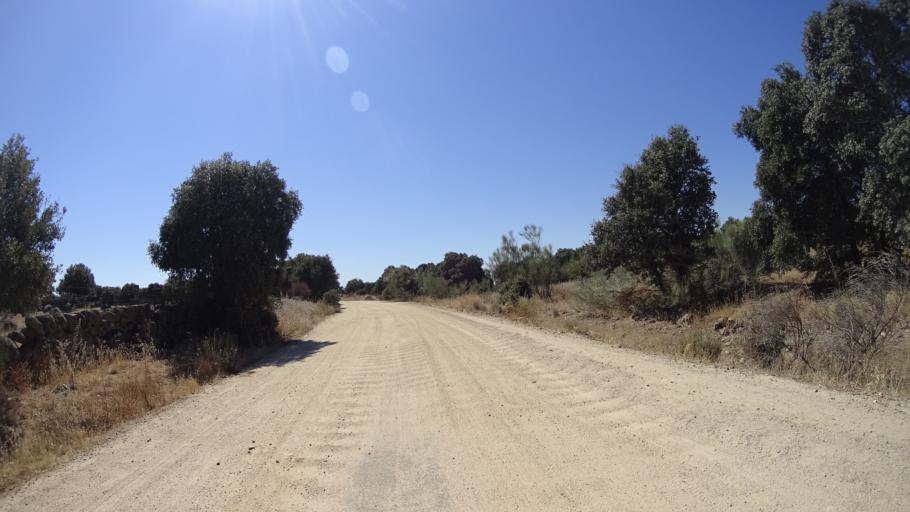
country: ES
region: Madrid
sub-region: Provincia de Madrid
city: Colmenarejo
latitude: 40.5312
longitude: -4.0107
